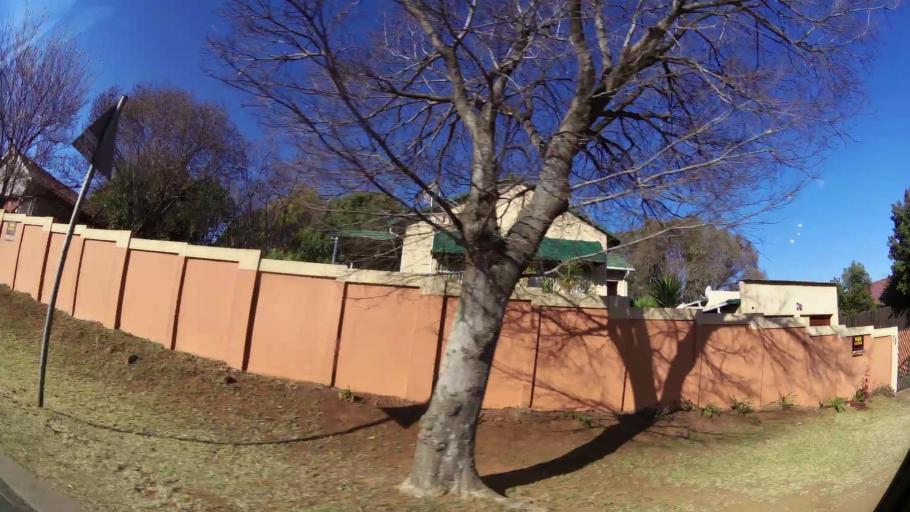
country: ZA
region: Gauteng
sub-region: City of Johannesburg Metropolitan Municipality
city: Johannesburg
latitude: -26.2917
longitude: 28.0540
